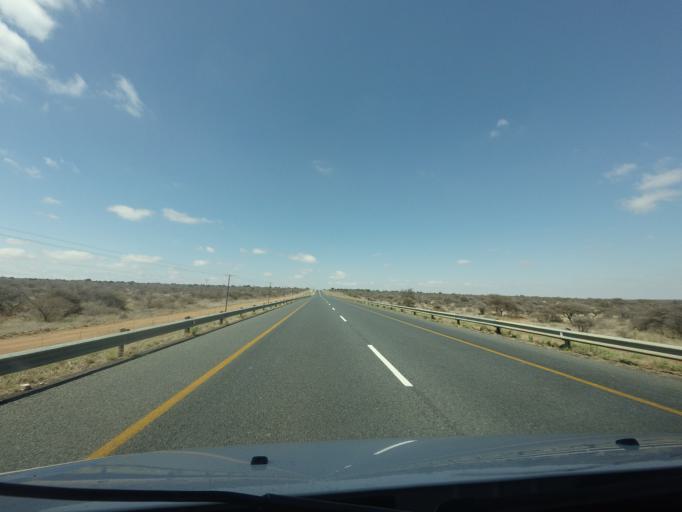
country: ZA
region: Limpopo
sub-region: Vhembe District Municipality
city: Louis Trichardt
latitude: -23.3940
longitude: 29.7618
